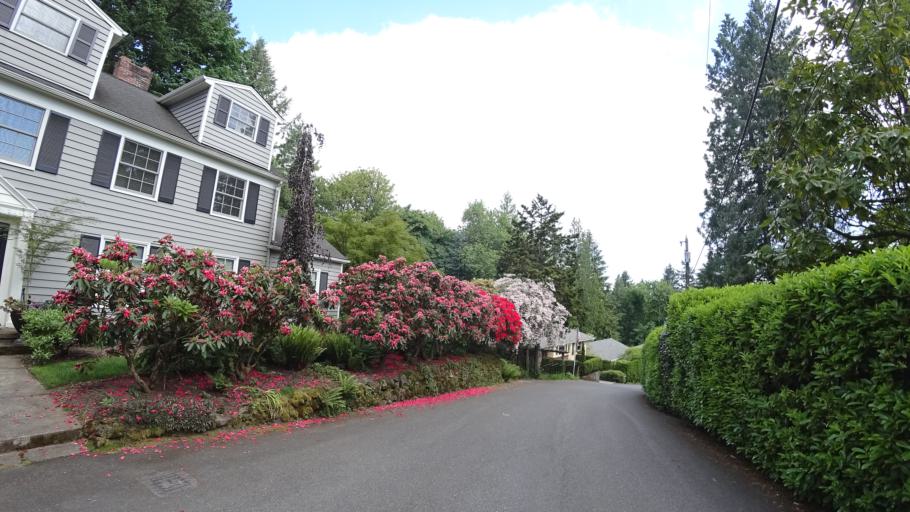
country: US
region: Oregon
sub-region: Multnomah County
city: Portland
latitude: 45.5041
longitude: -122.7105
